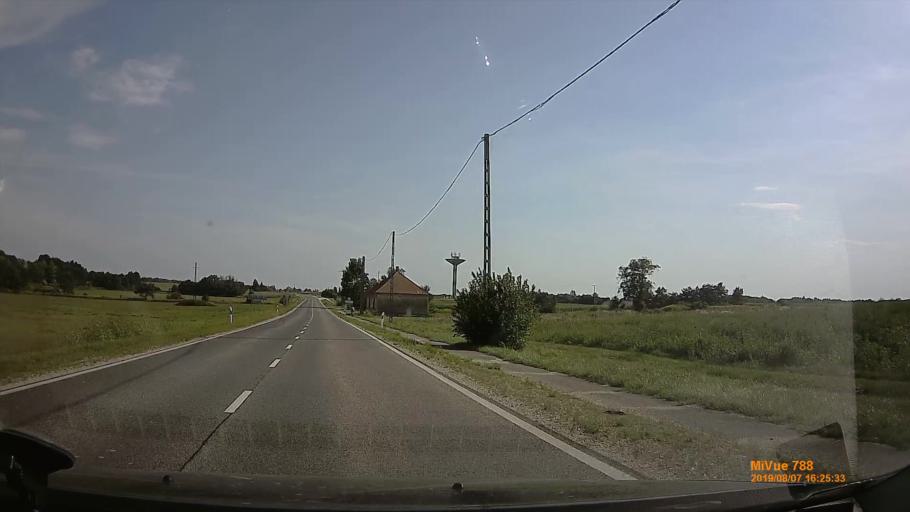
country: HU
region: Zala
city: Lenti
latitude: 46.7213
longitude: 16.5497
